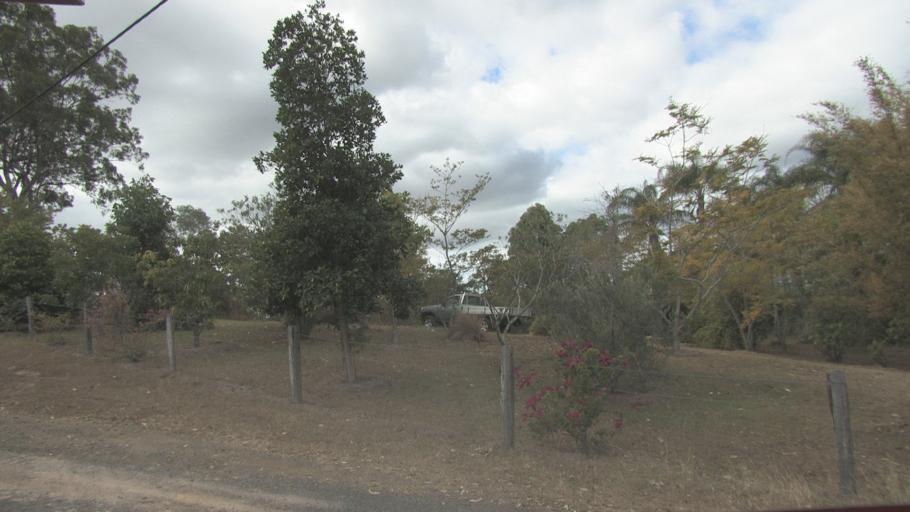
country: AU
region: Queensland
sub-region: Logan
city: Cedar Vale
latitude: -27.9028
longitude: 153.0387
